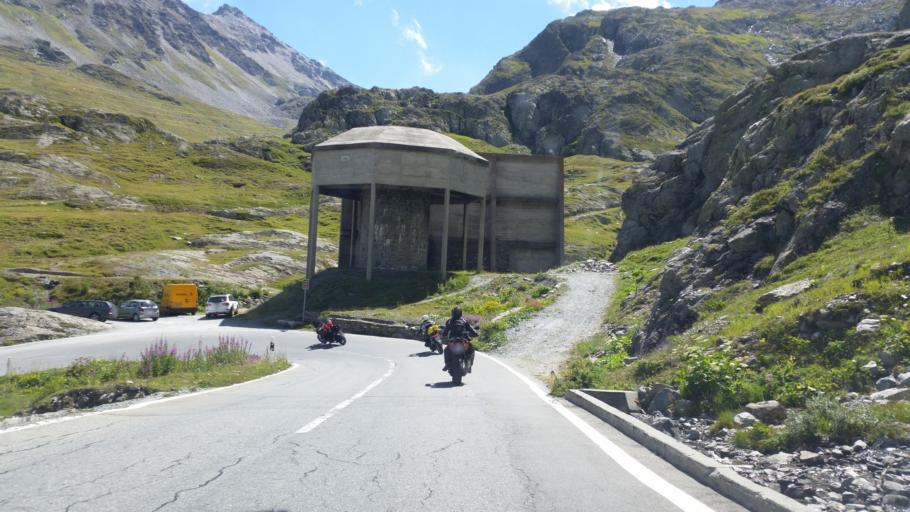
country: IT
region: Aosta Valley
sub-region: Valle d'Aosta
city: San Leonardo
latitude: 45.8742
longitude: 7.1803
